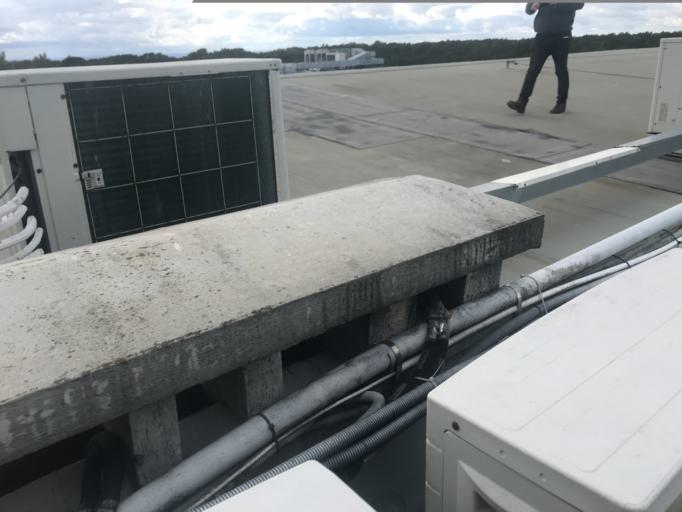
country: PL
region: Pomeranian Voivodeship
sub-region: Powiat pucki
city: Jastarnia
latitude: 54.6853
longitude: 18.7172
